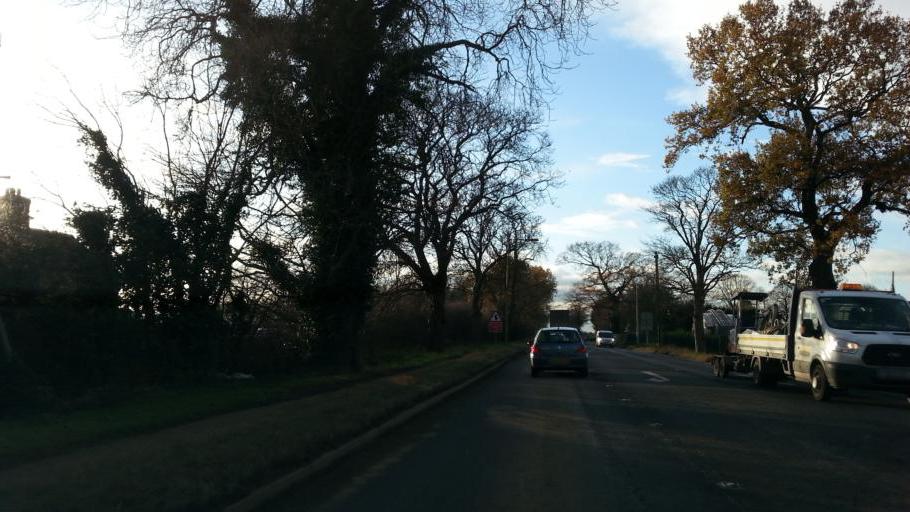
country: GB
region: England
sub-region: Peterborough
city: Thorney
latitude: 52.6174
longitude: -0.1410
